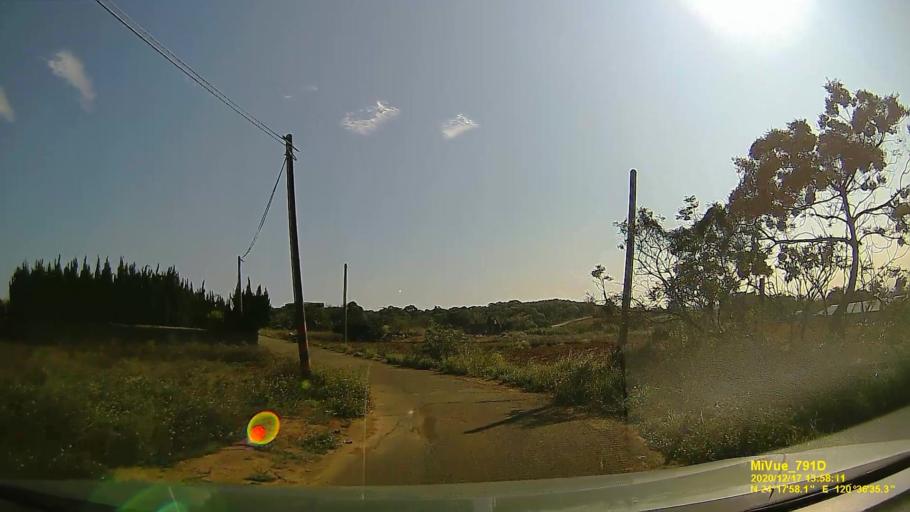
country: TW
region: Taiwan
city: Fengyuan
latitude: 24.2995
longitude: 120.6098
